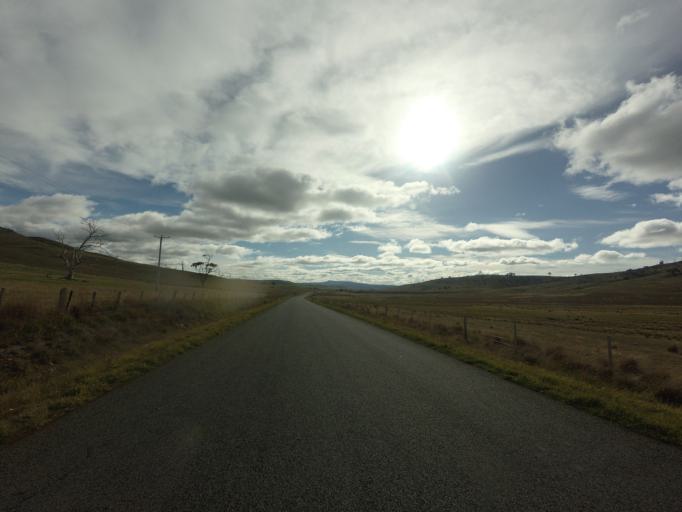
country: AU
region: Tasmania
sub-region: Brighton
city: Bridgewater
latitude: -42.3727
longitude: 147.3556
